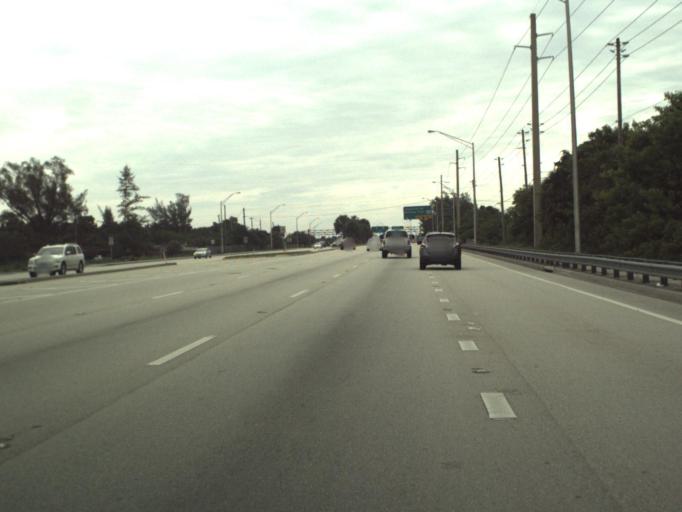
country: US
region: Florida
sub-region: Palm Beach County
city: Royal Palm Estates
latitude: 26.6781
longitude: -80.1302
